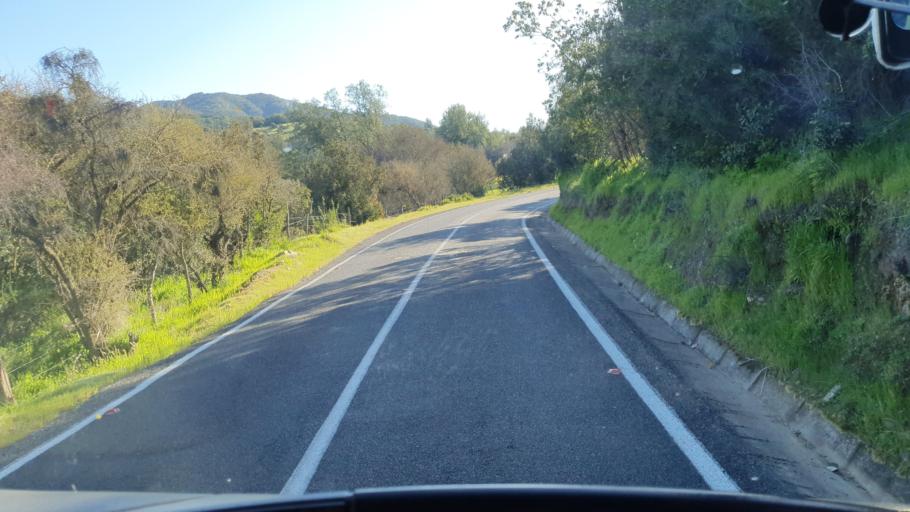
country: CL
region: Valparaiso
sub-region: Provincia de Marga Marga
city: Limache
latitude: -33.1986
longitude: -71.2253
